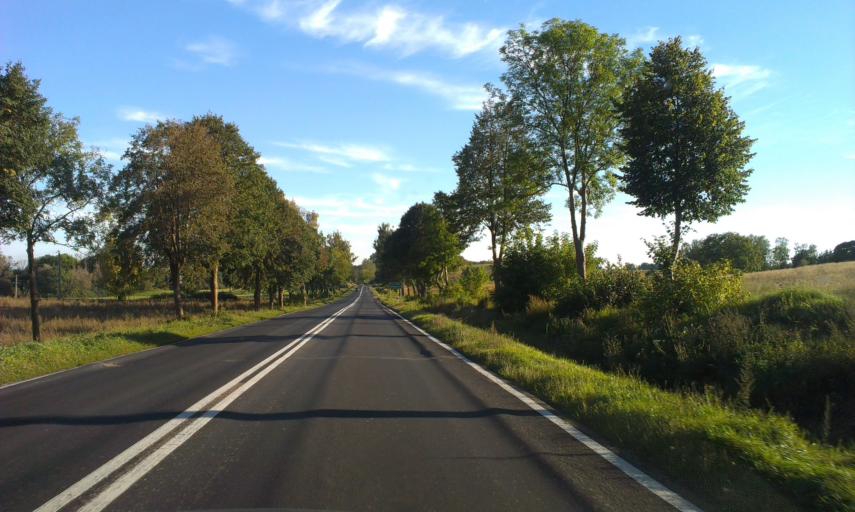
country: PL
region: West Pomeranian Voivodeship
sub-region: Powiat szczecinecki
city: Szczecinek
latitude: 53.7653
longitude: 16.6470
